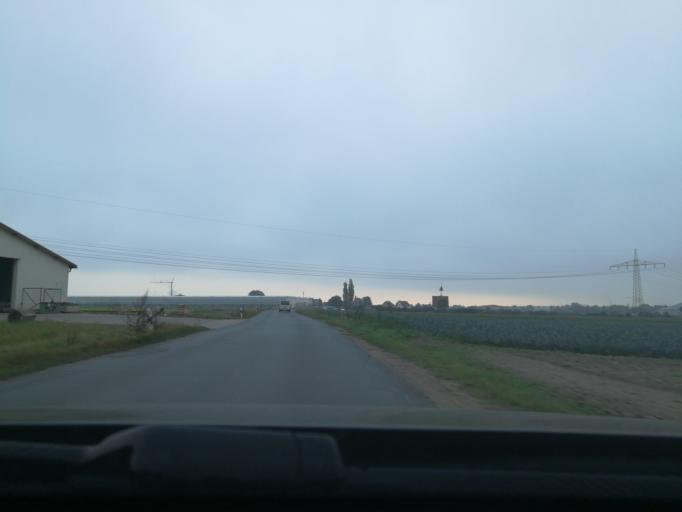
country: DE
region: Bavaria
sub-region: Regierungsbezirk Mittelfranken
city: Wetzendorf
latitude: 49.4877
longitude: 11.0219
